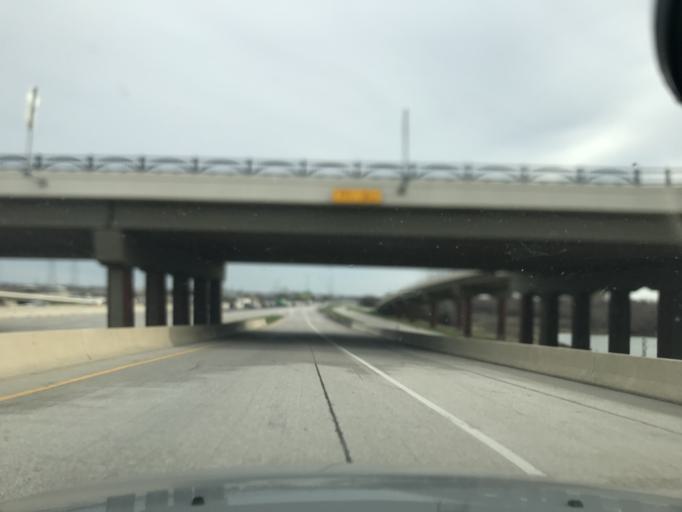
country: US
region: Texas
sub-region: Dallas County
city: Carrollton
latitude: 32.9787
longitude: -96.9279
